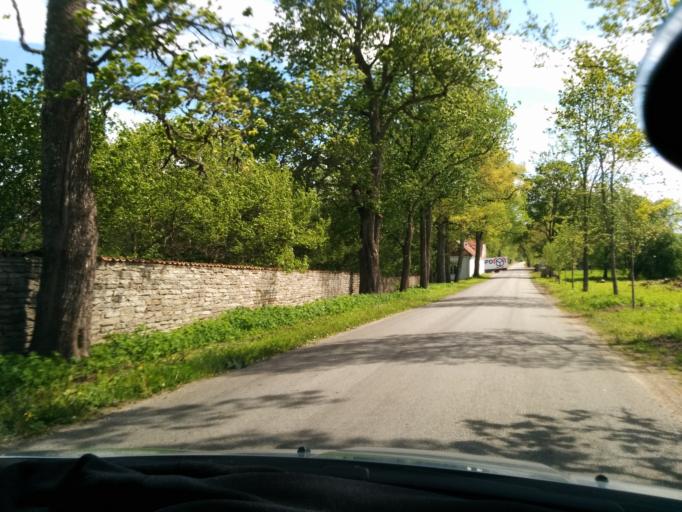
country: EE
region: Harju
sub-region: Loksa linn
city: Loksa
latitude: 59.5133
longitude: 25.9527
